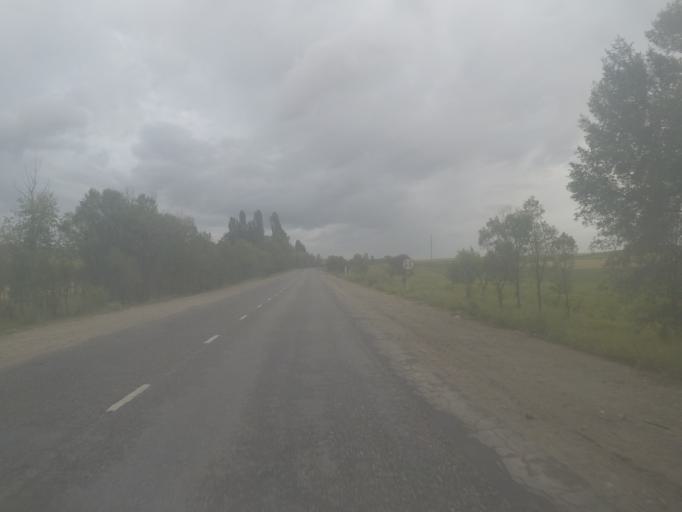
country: KG
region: Ysyk-Koel
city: Tyup
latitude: 42.6847
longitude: 78.3605
